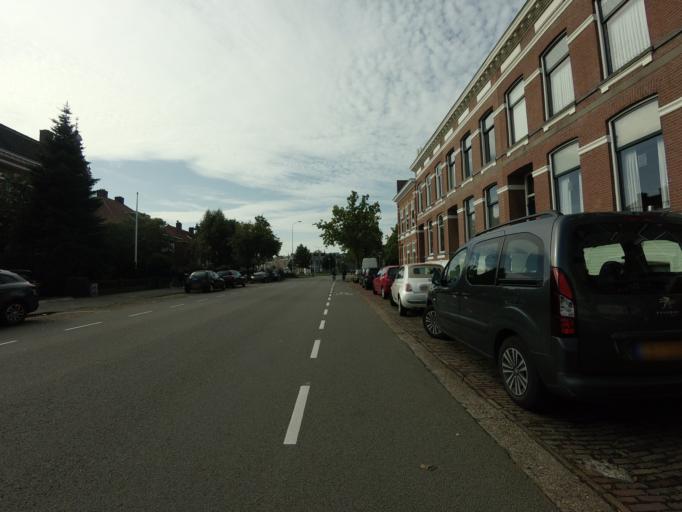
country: NL
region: North Brabant
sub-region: Gemeente Breda
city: Hoge Vucht
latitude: 51.5943
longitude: 4.7925
